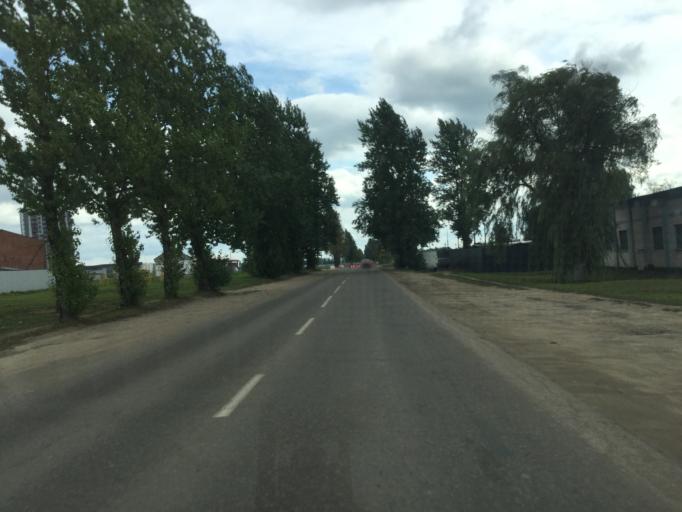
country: BY
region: Vitebsk
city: Vitebsk
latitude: 55.1684
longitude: 30.2513
